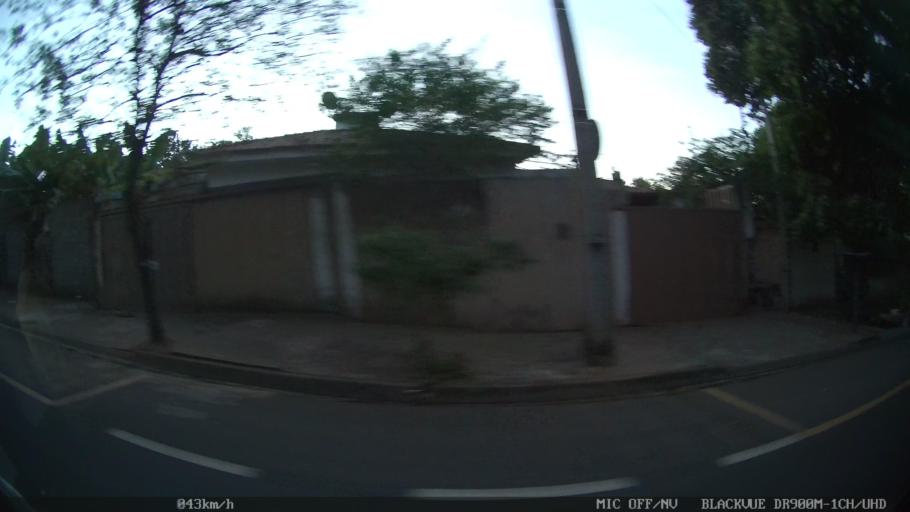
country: BR
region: Sao Paulo
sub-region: Catanduva
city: Catanduva
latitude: -21.1492
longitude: -48.9936
